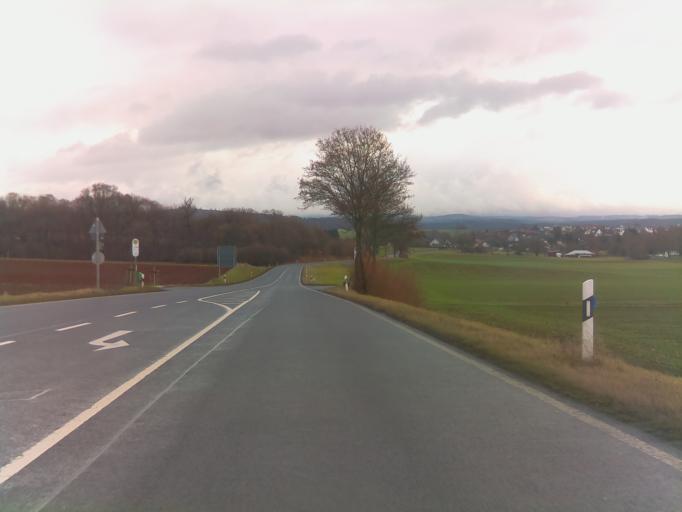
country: DE
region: Hesse
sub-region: Regierungsbezirk Giessen
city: Grunberg
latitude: 50.5519
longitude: 8.9371
